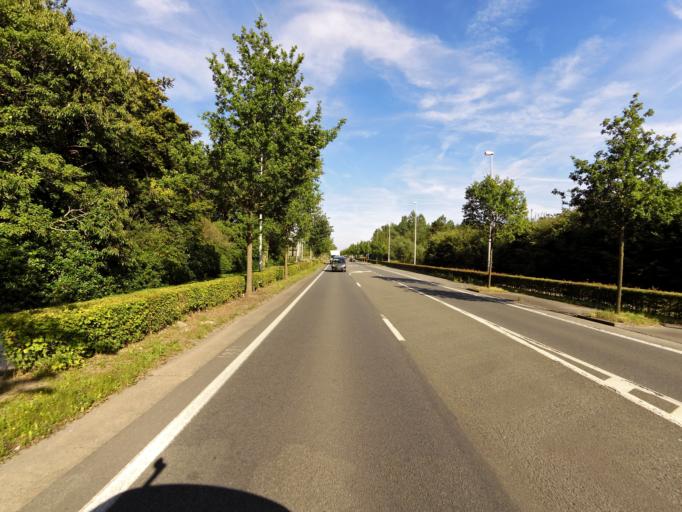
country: BE
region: Flanders
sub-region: Provincie West-Vlaanderen
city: Sint-Kruis
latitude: 51.2070
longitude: 3.2951
